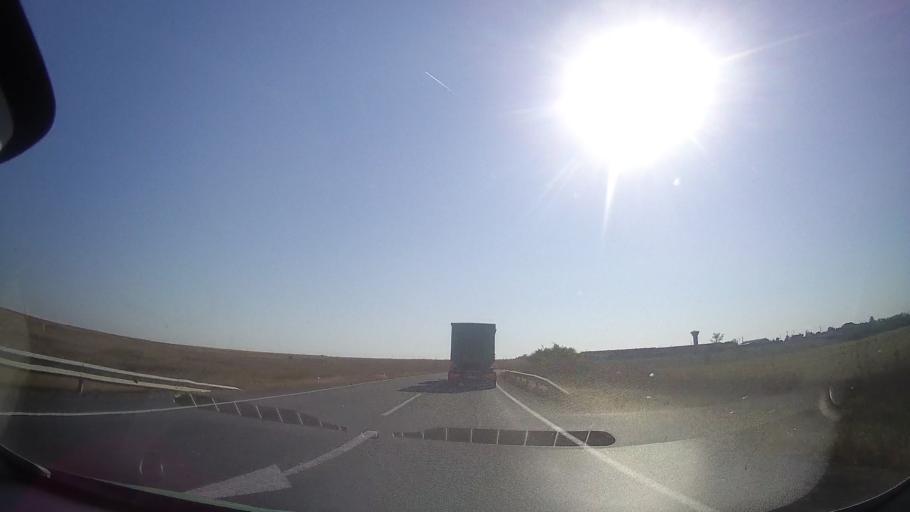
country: RO
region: Timis
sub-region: Comuna Ghizela
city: Ghizela
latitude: 45.7743
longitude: 21.7005
